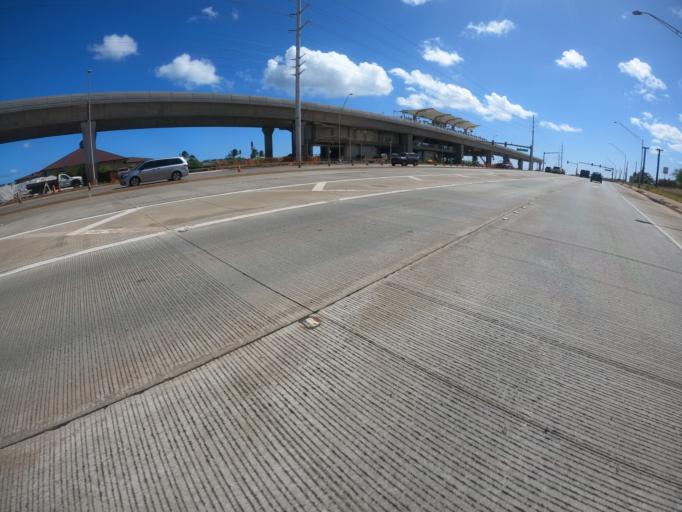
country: US
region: Hawaii
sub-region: Honolulu County
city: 'Ewa Villages
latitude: 21.3465
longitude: -158.0510
